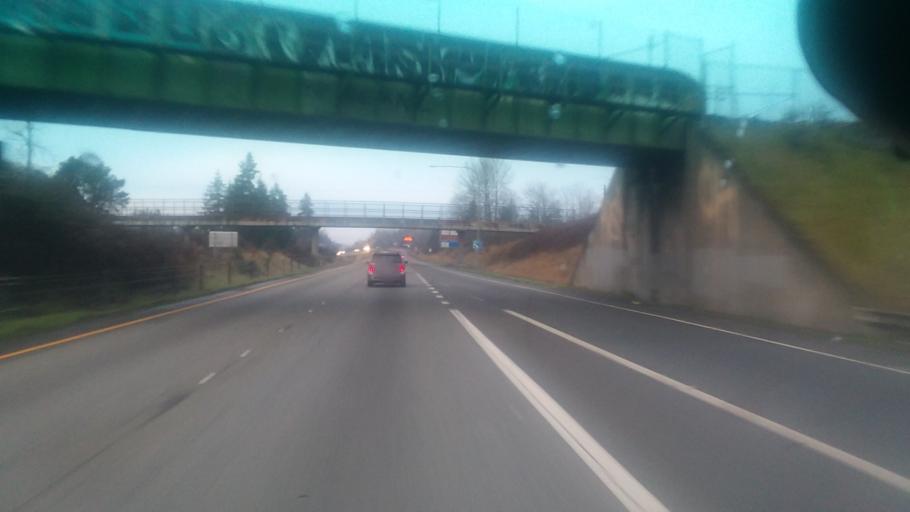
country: US
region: Washington
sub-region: Pierce County
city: Midland
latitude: 47.1592
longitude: -122.4054
